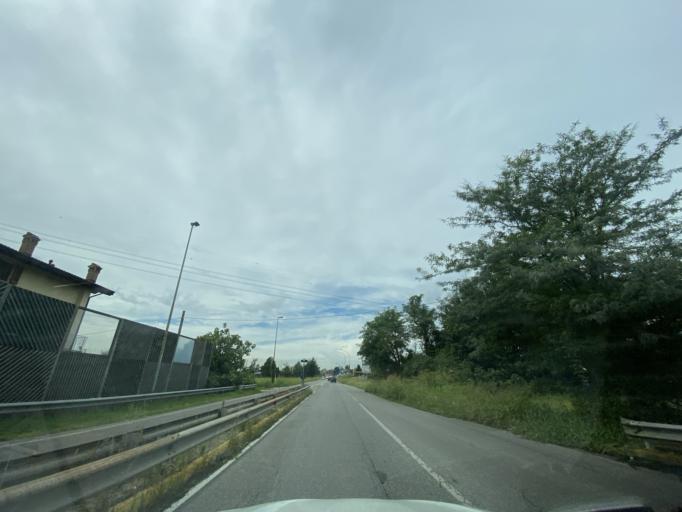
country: IT
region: Lombardy
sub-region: Citta metropolitana di Milano
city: Sant'Agata Martesana
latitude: 45.5226
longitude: 9.3792
